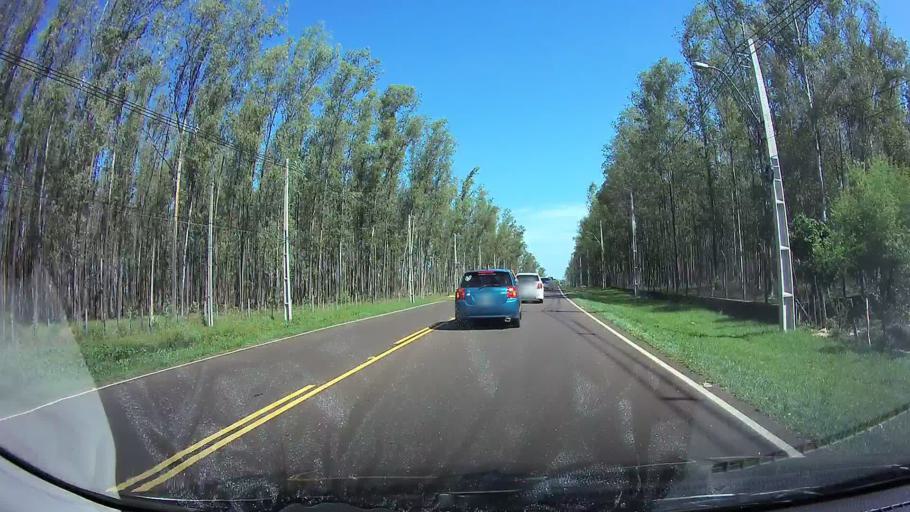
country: PY
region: Central
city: Ypacarai
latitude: -25.3745
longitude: -57.2629
